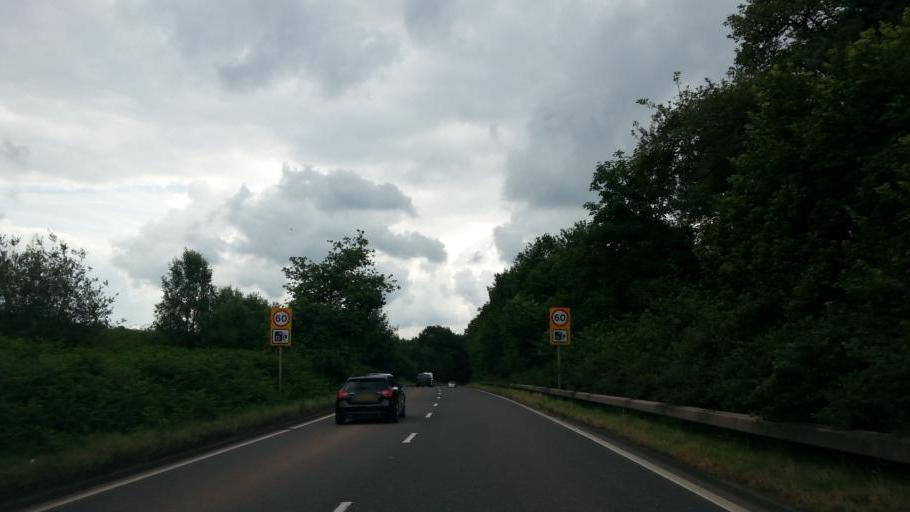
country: GB
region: England
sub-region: Staffordshire
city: Shenstone
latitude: 52.6133
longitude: -1.7974
